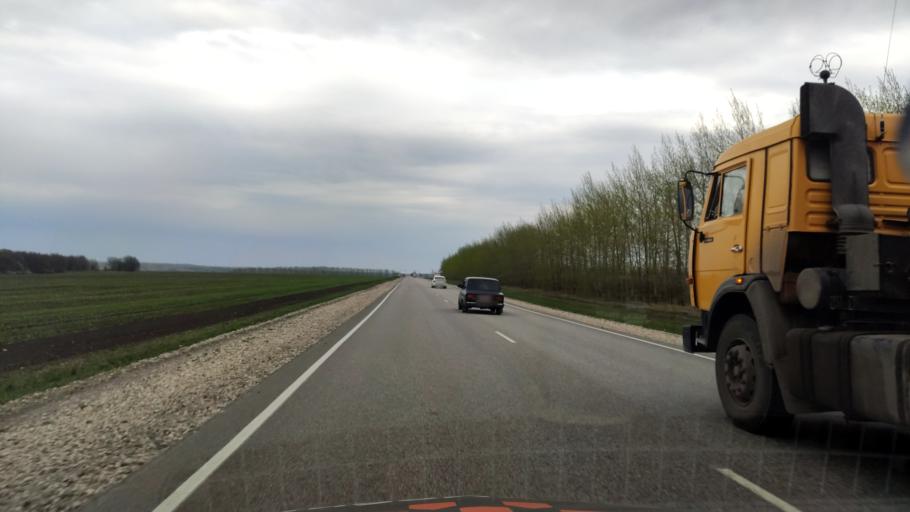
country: RU
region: Voronezj
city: Nizhnedevitsk
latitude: 51.5846
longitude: 38.5301
